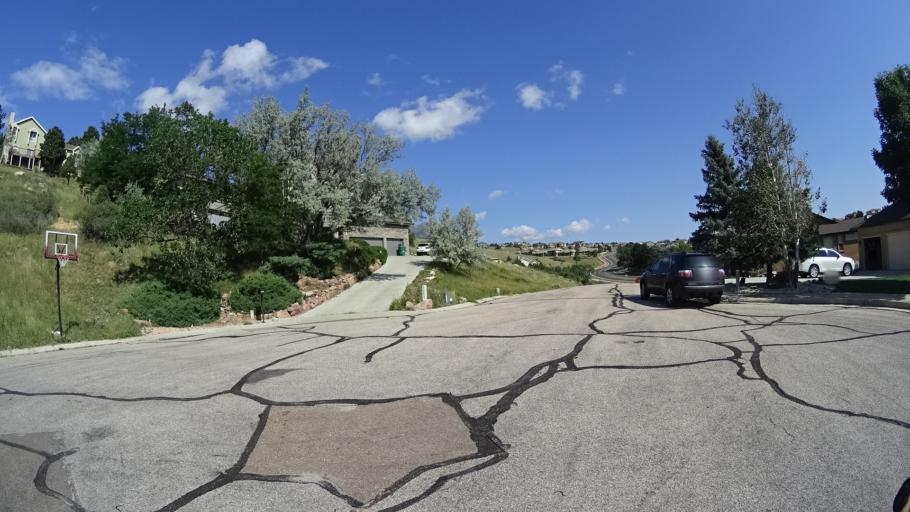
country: US
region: Colorado
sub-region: El Paso County
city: Manitou Springs
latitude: 38.9095
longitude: -104.8752
